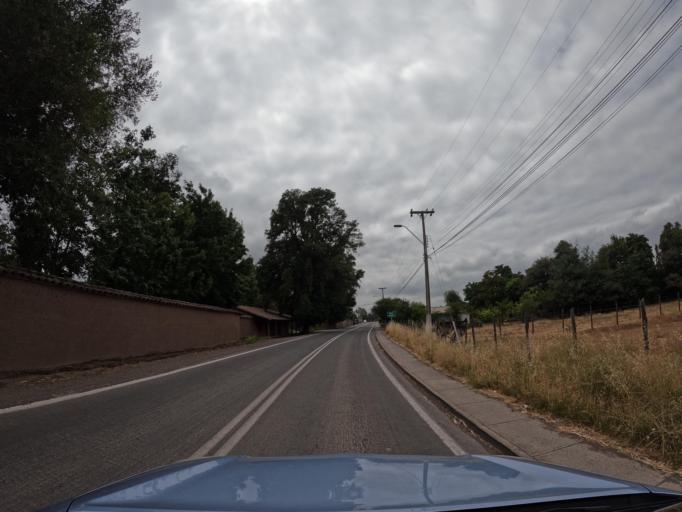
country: CL
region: Maule
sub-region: Provincia de Curico
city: Teno
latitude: -34.7589
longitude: -71.2048
